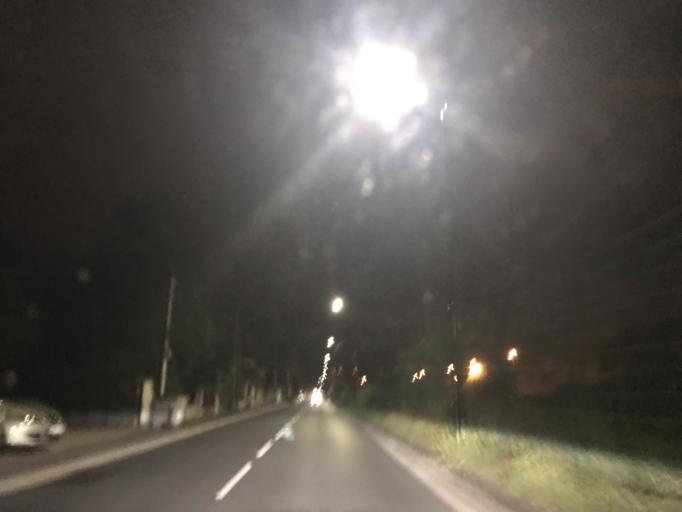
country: FR
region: Ile-de-France
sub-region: Departement des Yvelines
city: Sartrouville
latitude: 48.9399
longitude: 2.1948
